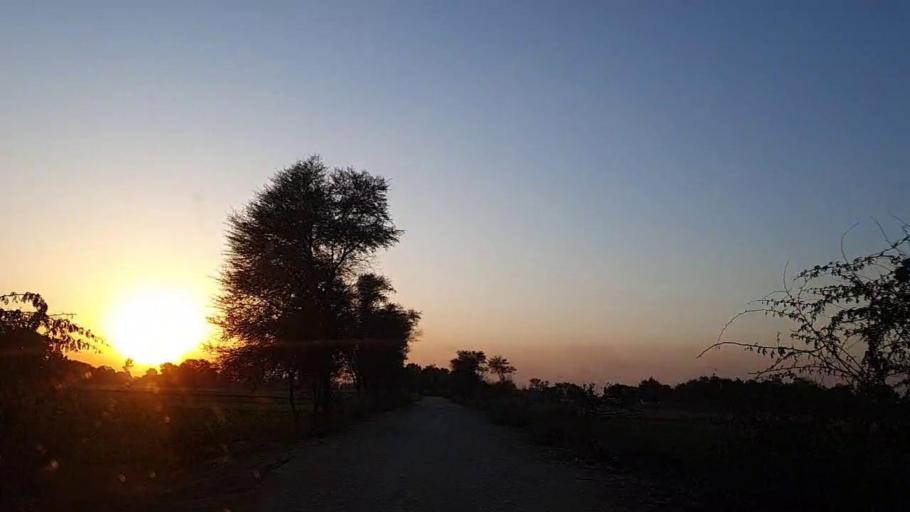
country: PK
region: Sindh
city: Daur
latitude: 26.3504
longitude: 68.3124
